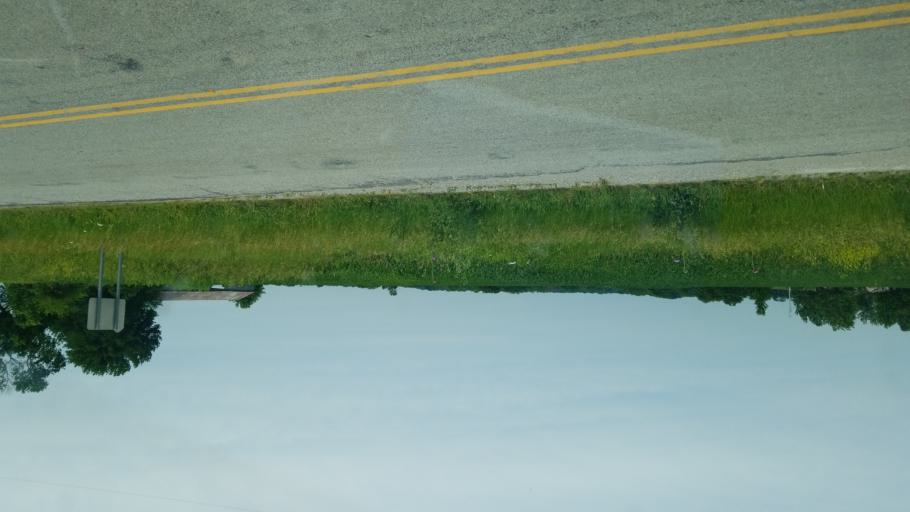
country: US
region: Missouri
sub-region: Saline County
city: Marshall
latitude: 38.9556
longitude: -93.0869
